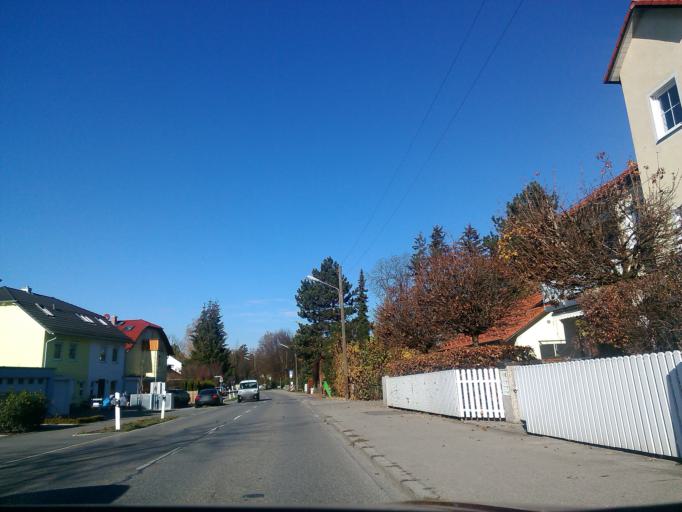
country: DE
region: Bavaria
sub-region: Upper Bavaria
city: Germering
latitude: 48.1678
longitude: 11.4109
